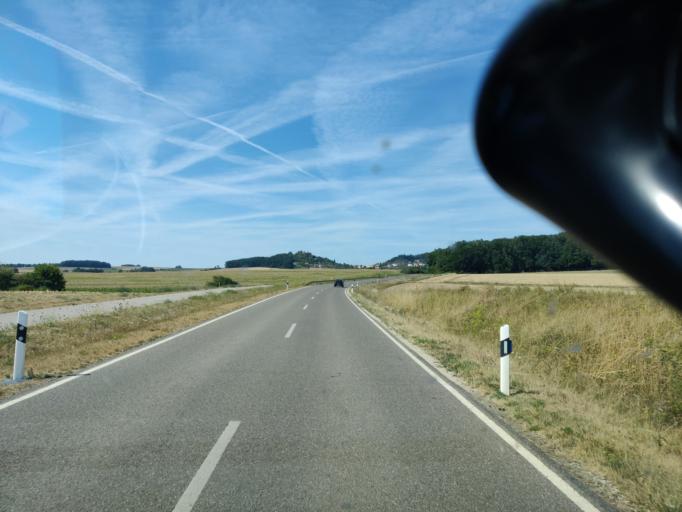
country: DE
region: Bavaria
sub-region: Regierungsbezirk Mittelfranken
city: Thalmassing
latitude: 49.0968
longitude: 11.2183
